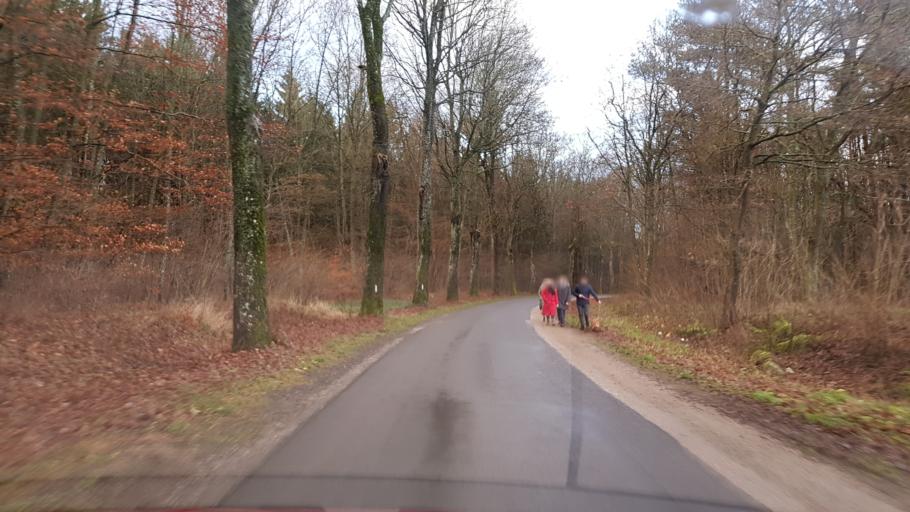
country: PL
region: West Pomeranian Voivodeship
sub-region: Powiat bialogardzki
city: Karlino
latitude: 53.9526
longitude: 15.9021
